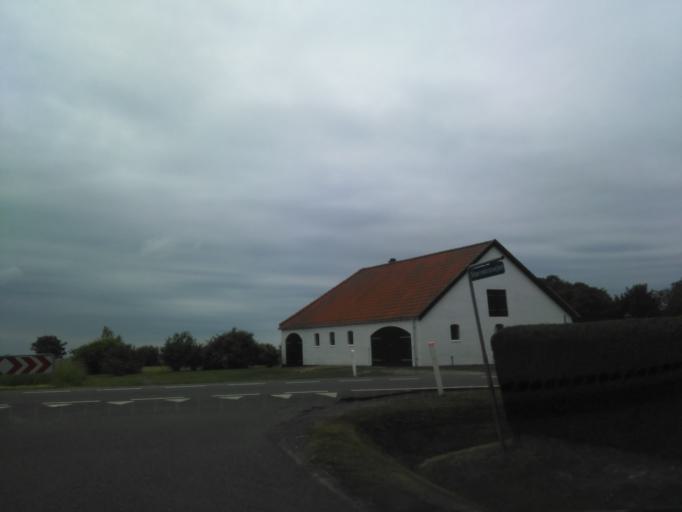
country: DK
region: Capital Region
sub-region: Bornholm Kommune
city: Akirkeby
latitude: 55.0893
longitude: 14.8778
